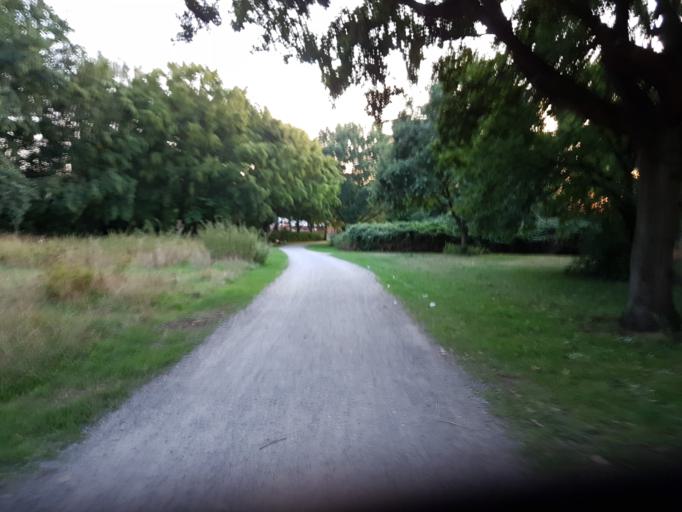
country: DE
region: Lower Saxony
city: Langenhagen
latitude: 52.4147
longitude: 9.7698
